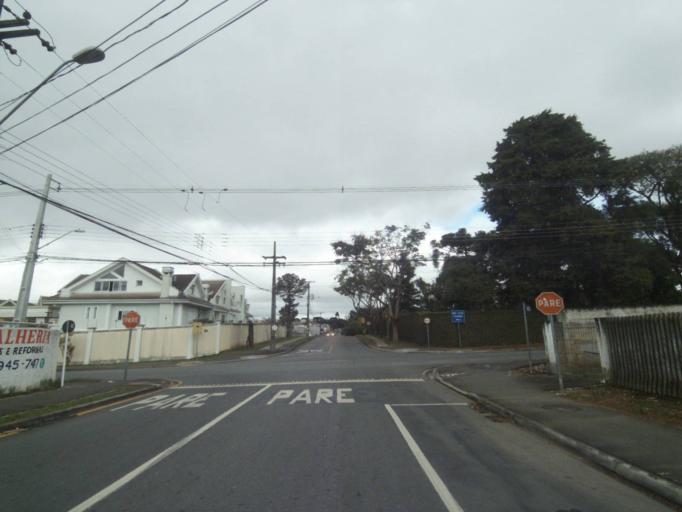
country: BR
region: Parana
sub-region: Curitiba
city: Curitiba
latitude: -25.5041
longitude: -49.2911
